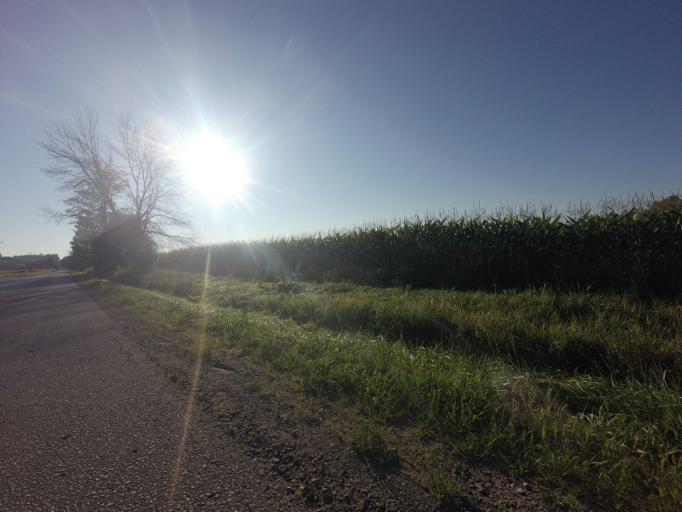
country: CA
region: Ontario
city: Bradford West Gwillimbury
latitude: 44.0383
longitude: -79.7913
